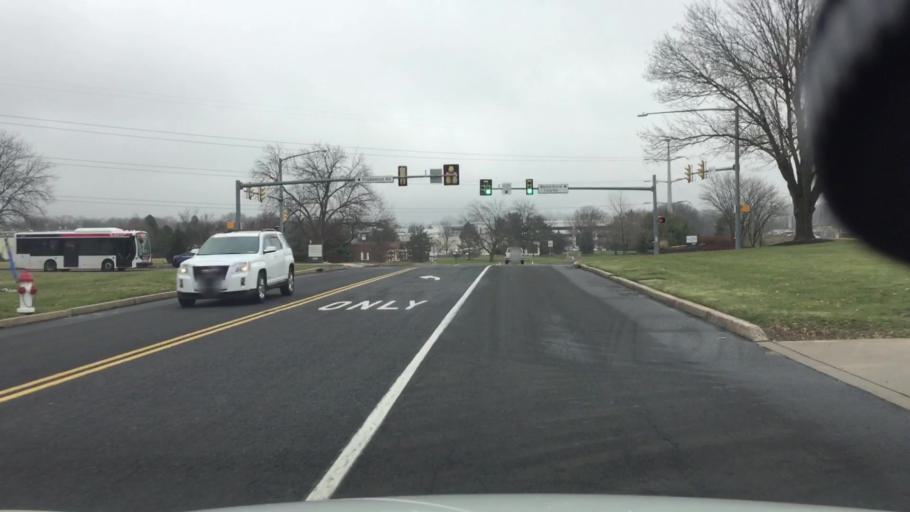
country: US
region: Pennsylvania
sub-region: Montgomery County
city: Horsham
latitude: 40.1685
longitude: -75.1395
